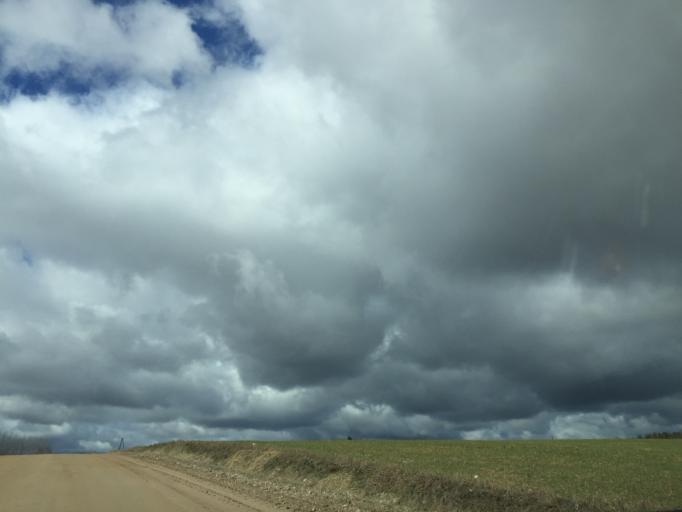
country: LV
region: Akniste
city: Akniste
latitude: 56.1058
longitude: 25.9521
